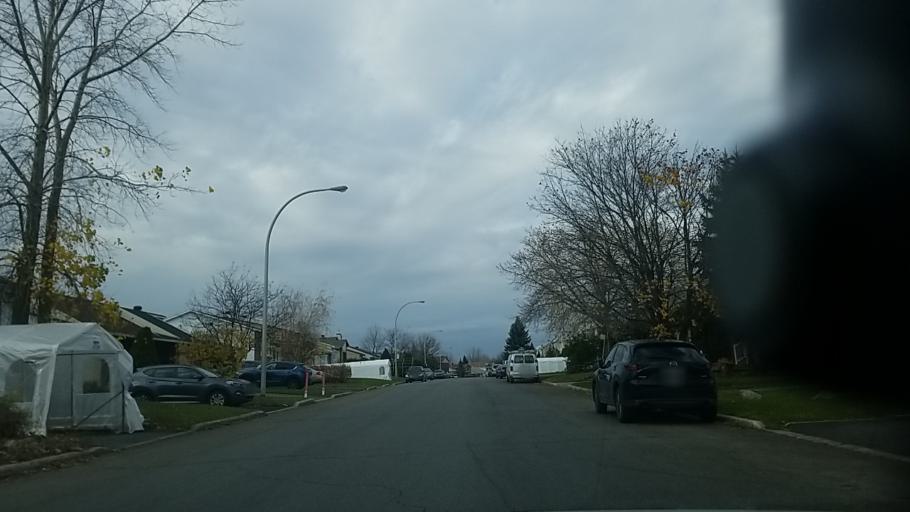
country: CA
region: Quebec
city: Dollard-Des Ormeaux
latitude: 45.5369
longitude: -73.7855
